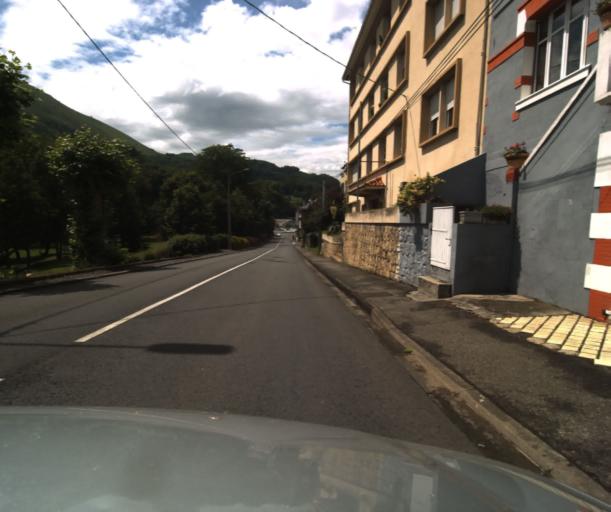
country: FR
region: Midi-Pyrenees
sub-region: Departement des Hautes-Pyrenees
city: Lourdes
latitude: 43.0893
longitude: -0.0514
